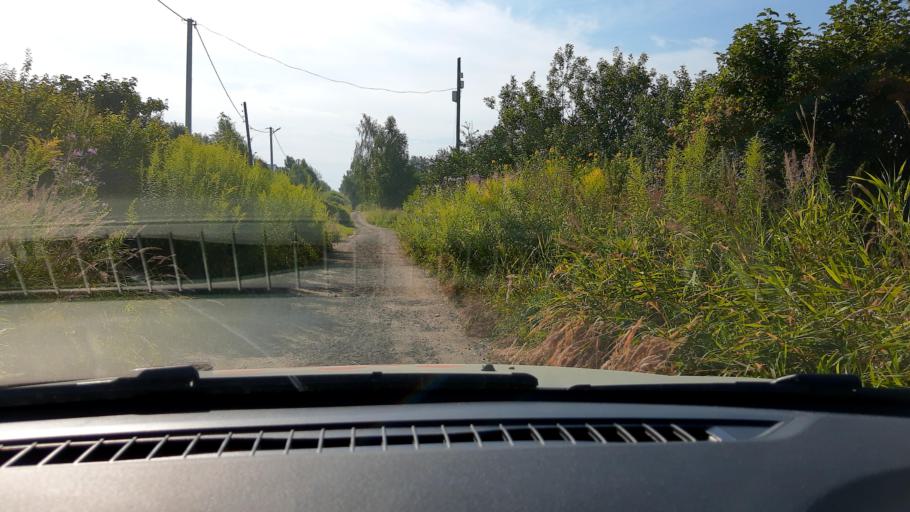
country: RU
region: Nizjnij Novgorod
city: Kstovo
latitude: 56.3097
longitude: 44.2703
